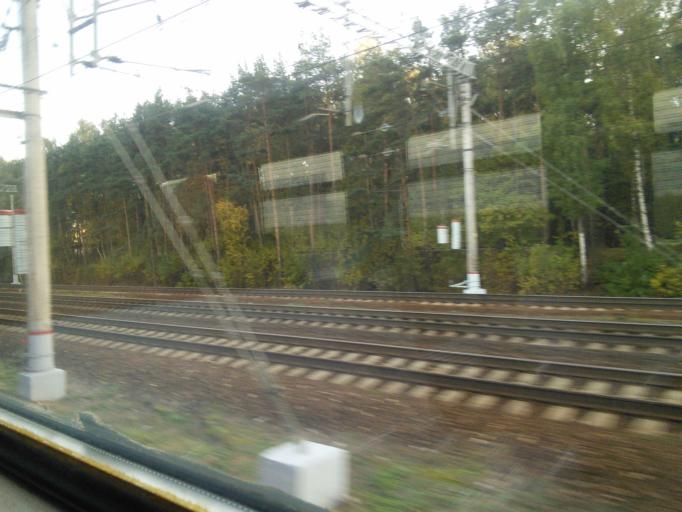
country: RU
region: Moskovskaya
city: Levoberezhnaya
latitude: 55.8839
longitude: 37.4763
